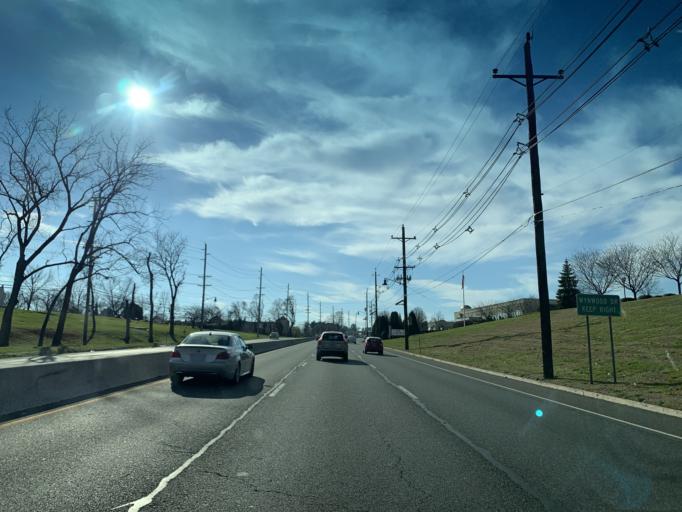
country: US
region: New Jersey
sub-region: Burlington County
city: Cinnaminson
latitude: 40.0024
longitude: -74.9839
